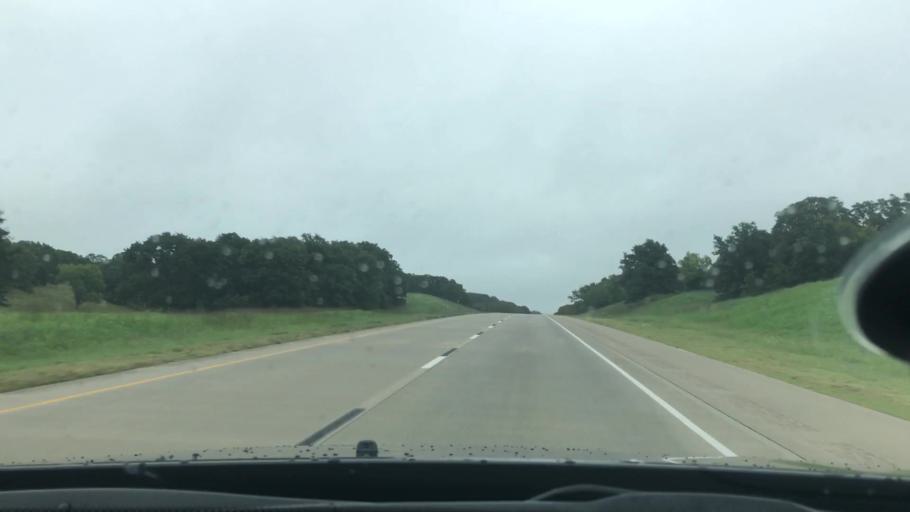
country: US
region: Oklahoma
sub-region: Lincoln County
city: Prague
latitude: 35.3846
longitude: -96.5843
